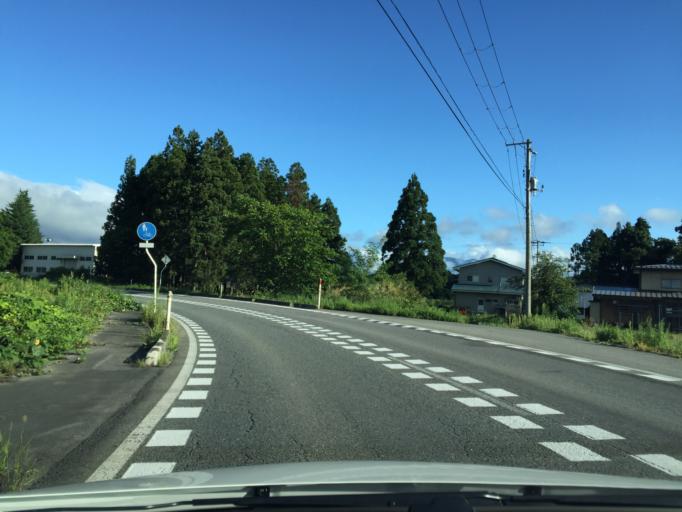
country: JP
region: Yamagata
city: Yonezawa
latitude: 37.9230
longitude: 140.1569
